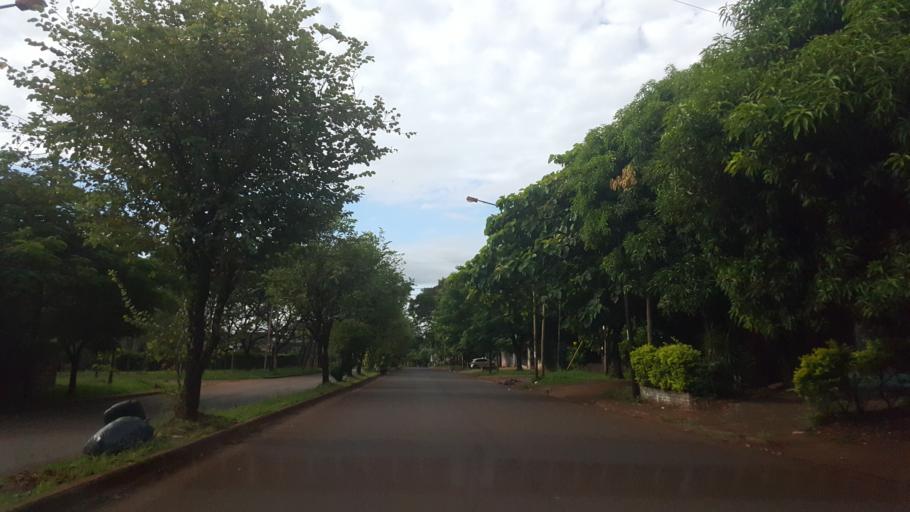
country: AR
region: Misiones
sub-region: Departamento de Capital
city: Posadas
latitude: -27.3995
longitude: -55.9361
